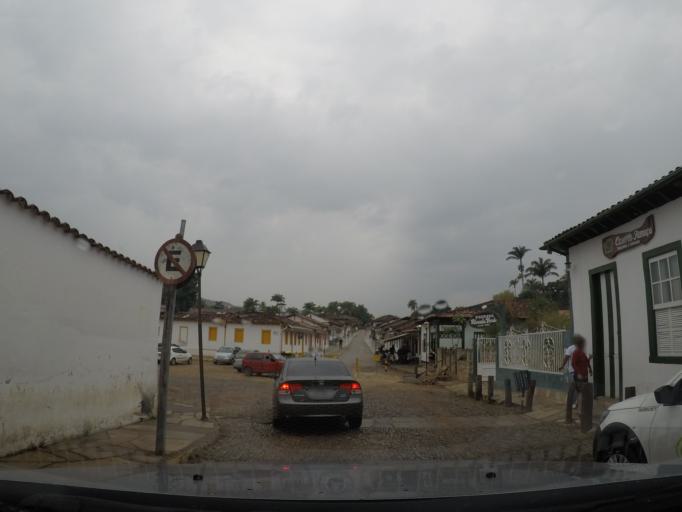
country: BR
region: Goias
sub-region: Pirenopolis
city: Pirenopolis
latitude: -15.8511
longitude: -48.9584
